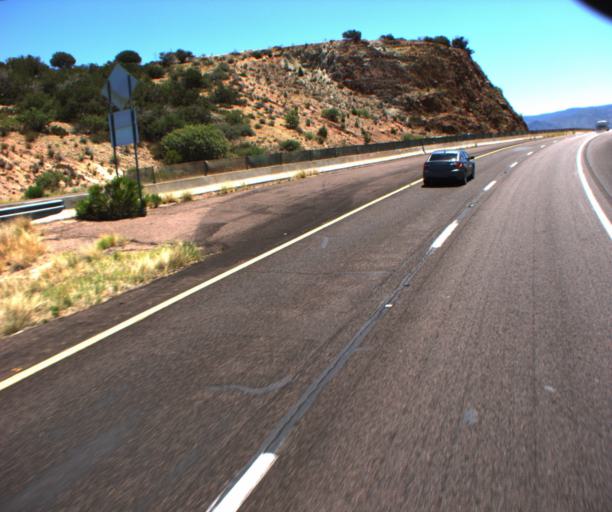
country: US
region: Arizona
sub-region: Gila County
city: Tonto Basin
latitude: 33.9918
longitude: -111.3783
